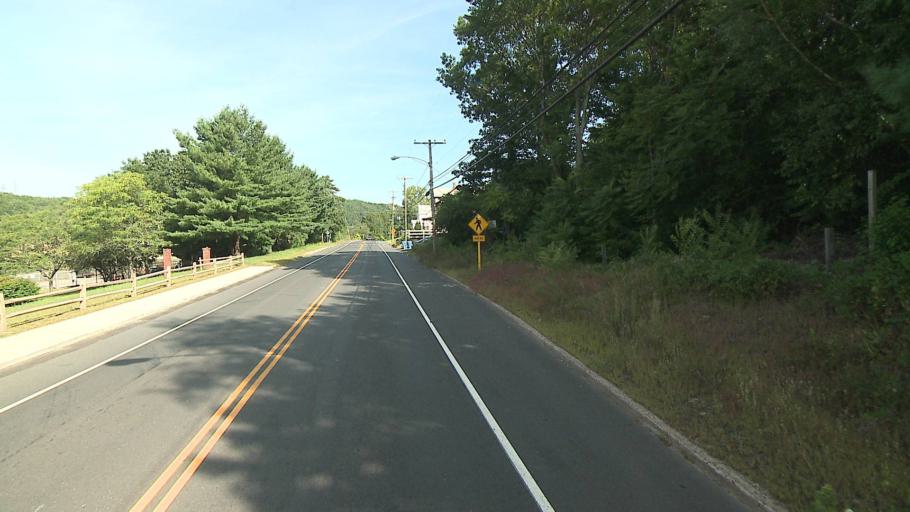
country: US
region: Connecticut
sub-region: Litchfield County
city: Oakville
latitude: 41.5942
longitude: -73.0564
